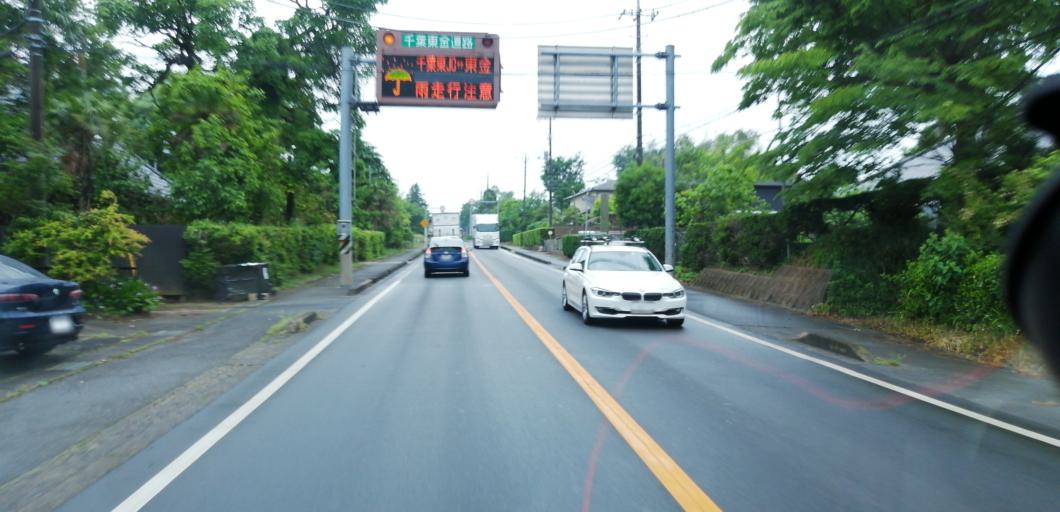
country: JP
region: Chiba
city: Oami
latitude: 35.5747
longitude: 140.2661
